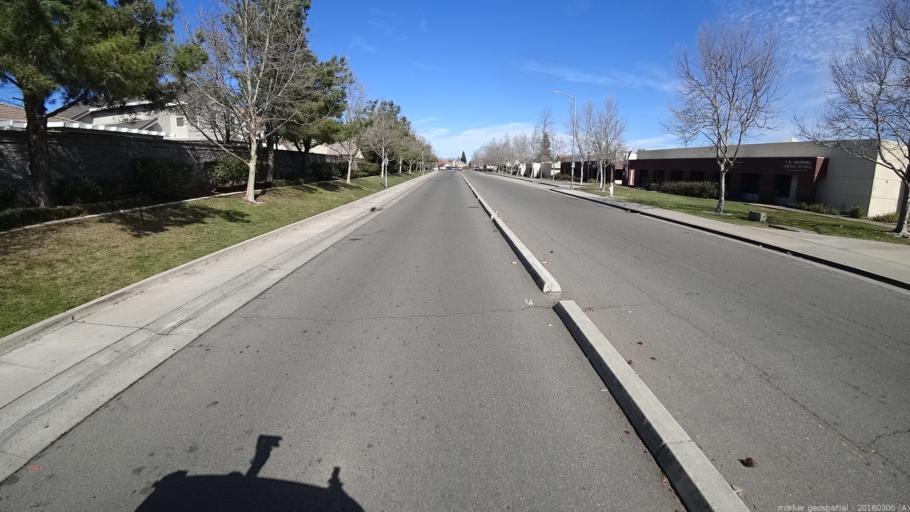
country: US
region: California
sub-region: Sacramento County
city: Vineyard
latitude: 38.4584
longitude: -121.3486
